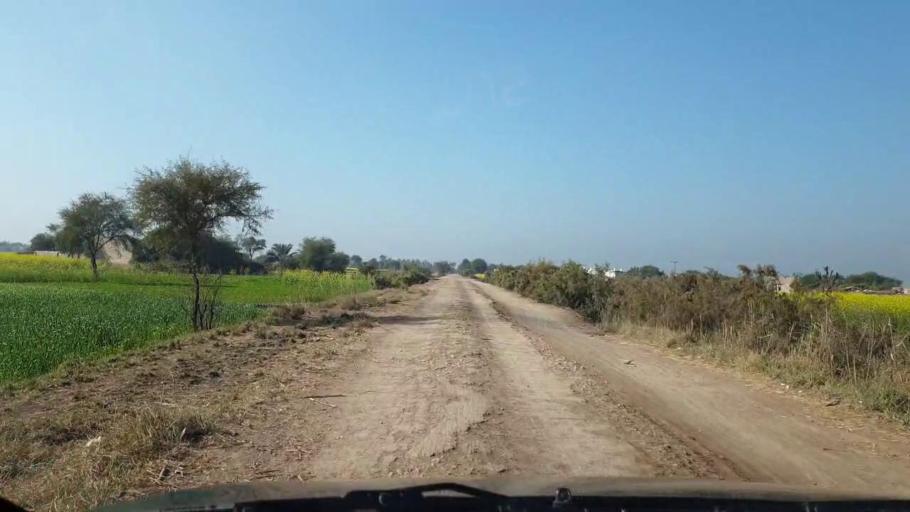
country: PK
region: Sindh
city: Sinjhoro
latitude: 26.0033
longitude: 68.7725
